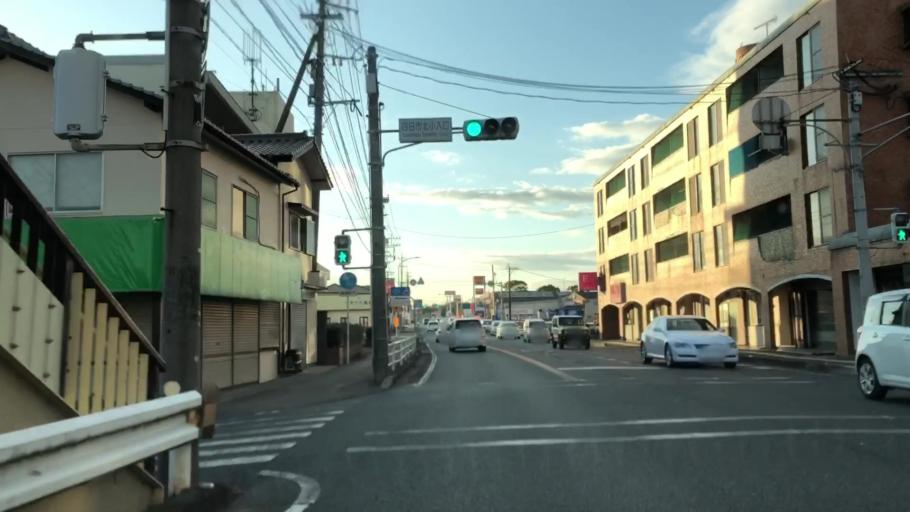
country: JP
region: Oita
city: Bungo-Takada-shi
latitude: 33.5347
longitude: 131.3272
